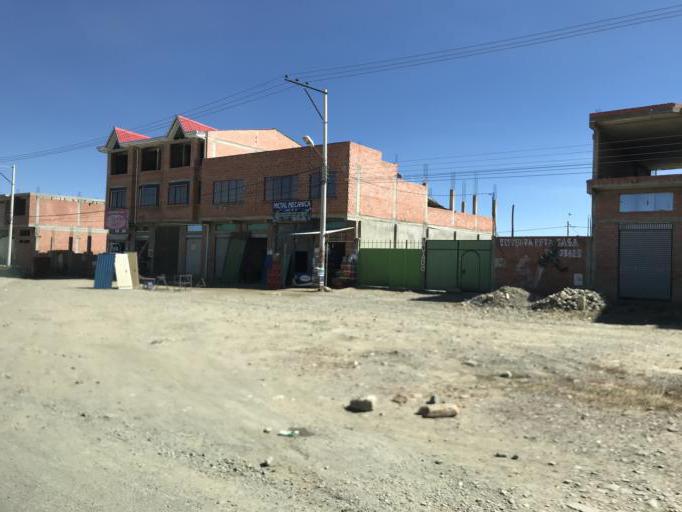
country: BO
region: La Paz
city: La Paz
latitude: -16.5078
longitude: -68.2614
